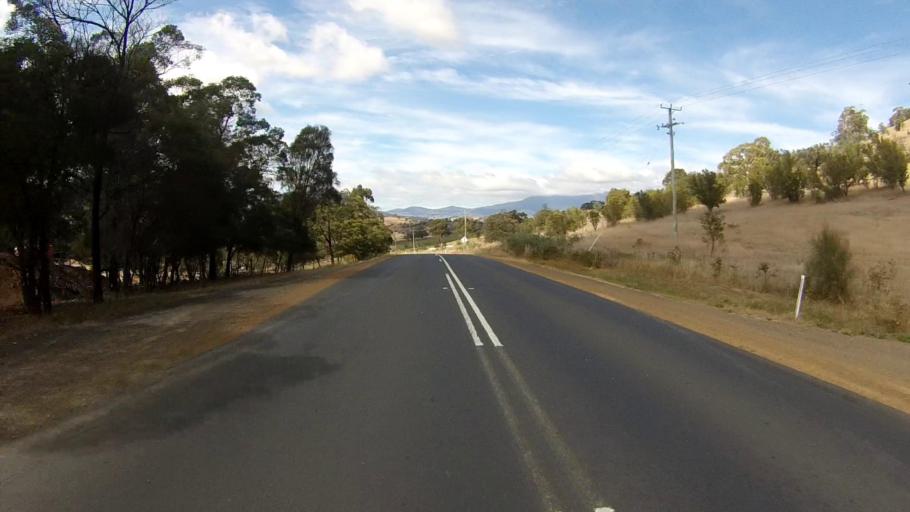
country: AU
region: Tasmania
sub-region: Brighton
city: Old Beach
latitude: -42.7297
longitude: 147.2886
